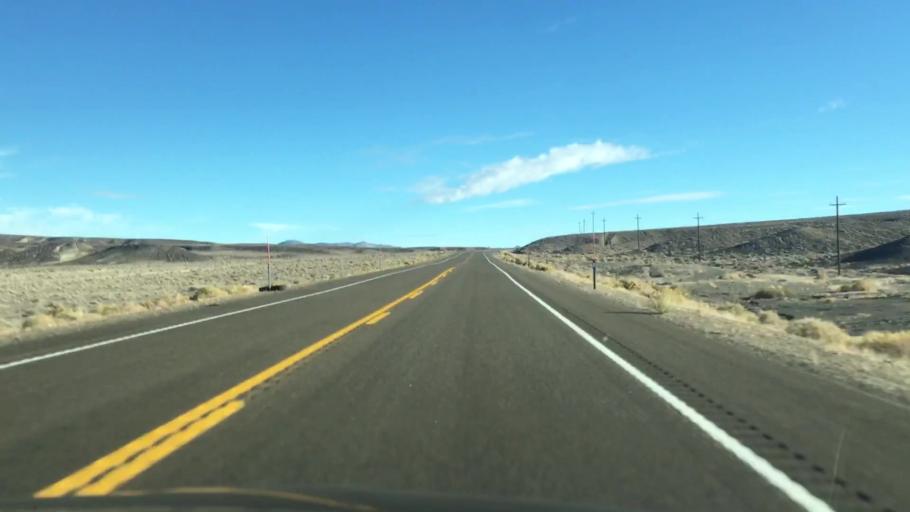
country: US
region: Nevada
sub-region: Mineral County
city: Hawthorne
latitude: 38.2329
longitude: -118.0226
